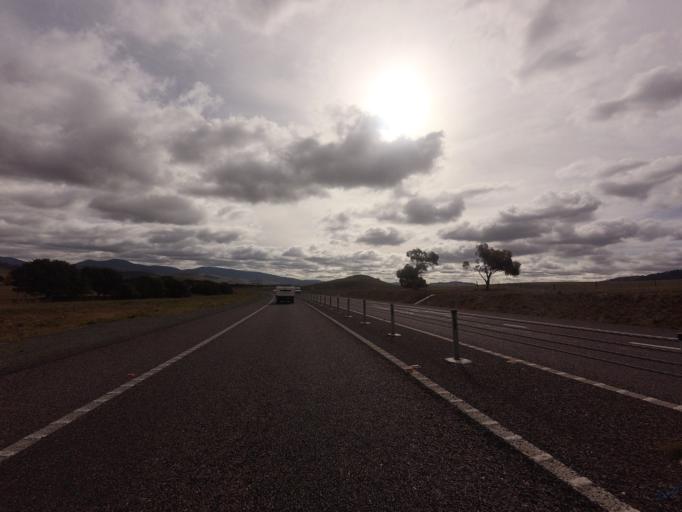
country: AU
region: Tasmania
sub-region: Brighton
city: Bridgewater
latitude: -42.5274
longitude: 147.2016
